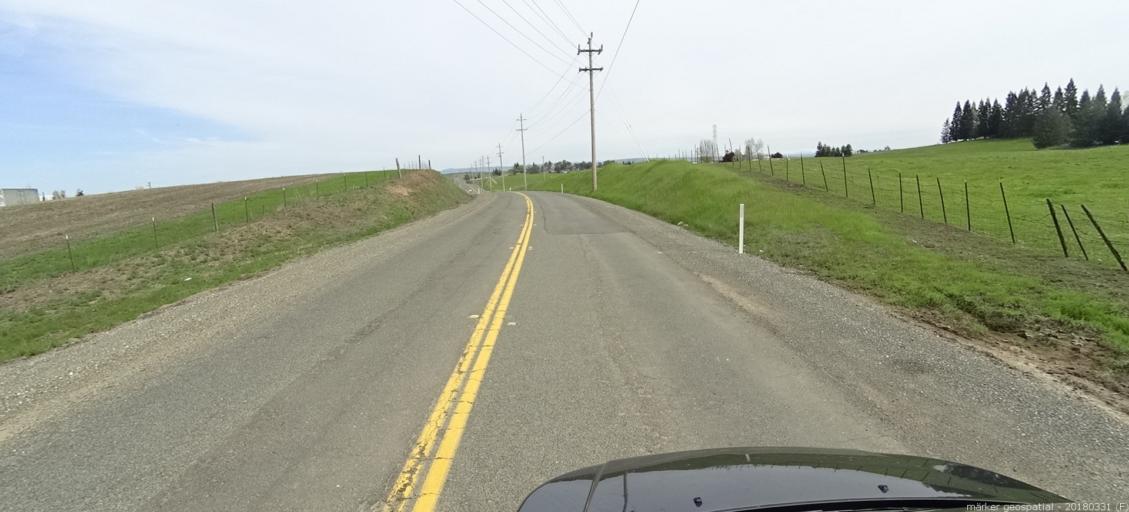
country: US
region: California
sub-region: Sacramento County
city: Rancho Murieta
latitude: 38.4978
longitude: -121.1456
